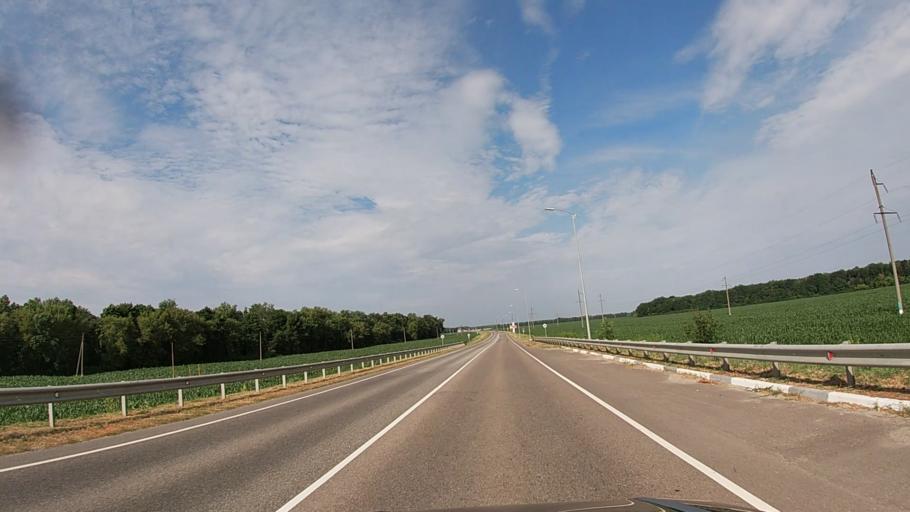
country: RU
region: Belgorod
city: Proletarskiy
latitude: 50.8014
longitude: 35.7335
